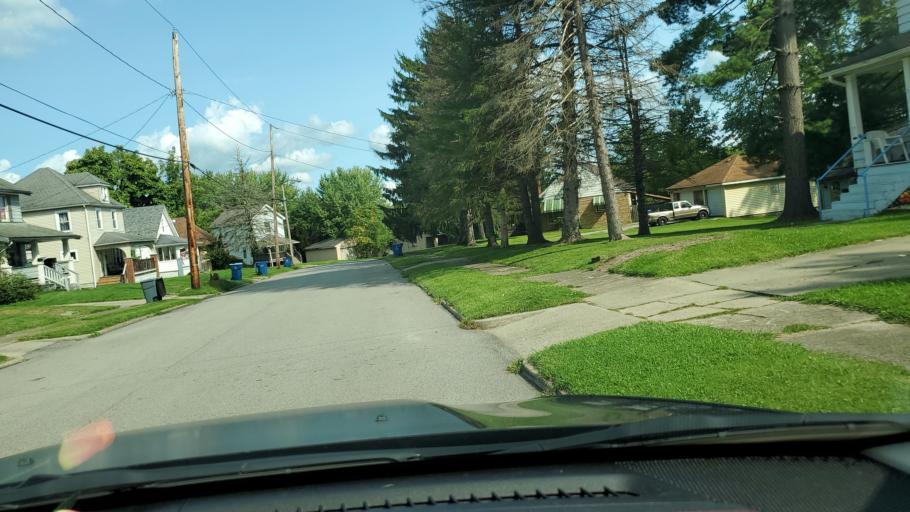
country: US
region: Ohio
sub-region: Mahoning County
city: Struthers
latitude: 41.0521
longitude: -80.5874
